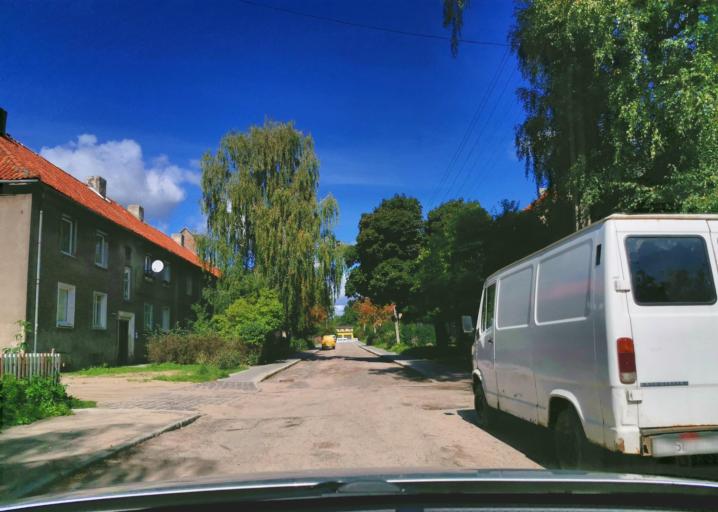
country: RU
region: Kaliningrad
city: Chernyakhovsk
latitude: 54.6359
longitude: 21.8402
